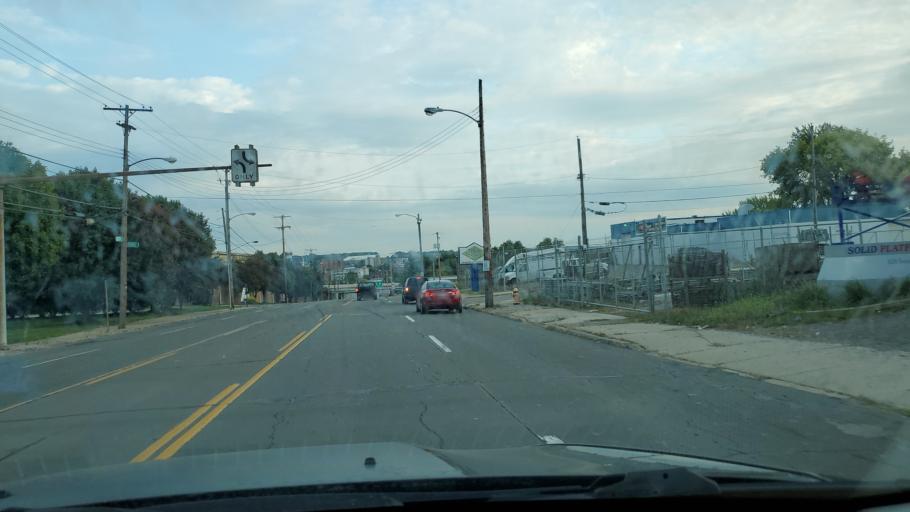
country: US
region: Ohio
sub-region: Mahoning County
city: Youngstown
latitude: 41.0893
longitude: -80.6463
